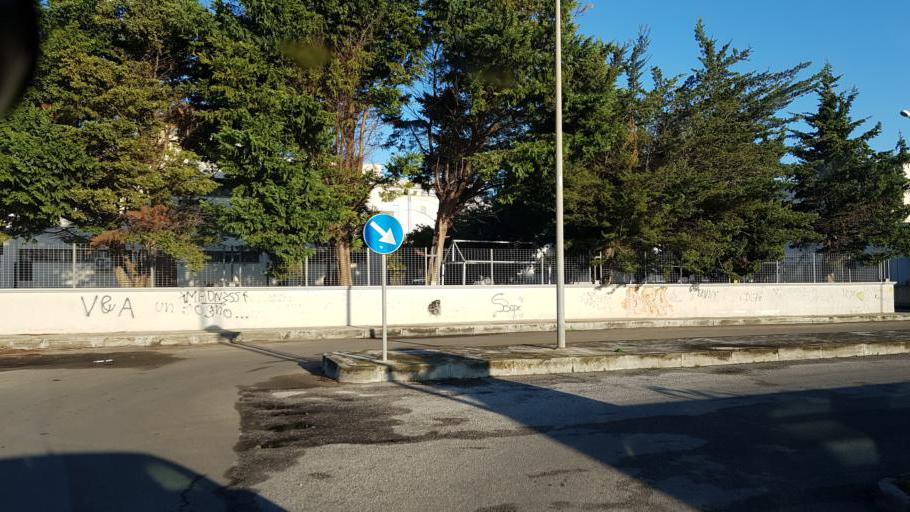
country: IT
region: Apulia
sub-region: Provincia di Brindisi
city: Brindisi
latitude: 40.6213
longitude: 17.9414
